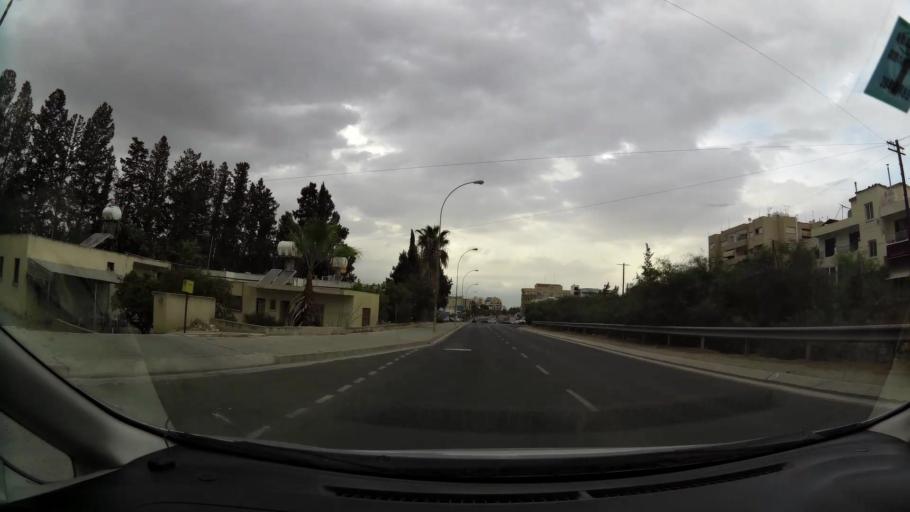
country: CY
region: Lefkosia
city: Nicosia
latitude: 35.1401
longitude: 33.3583
